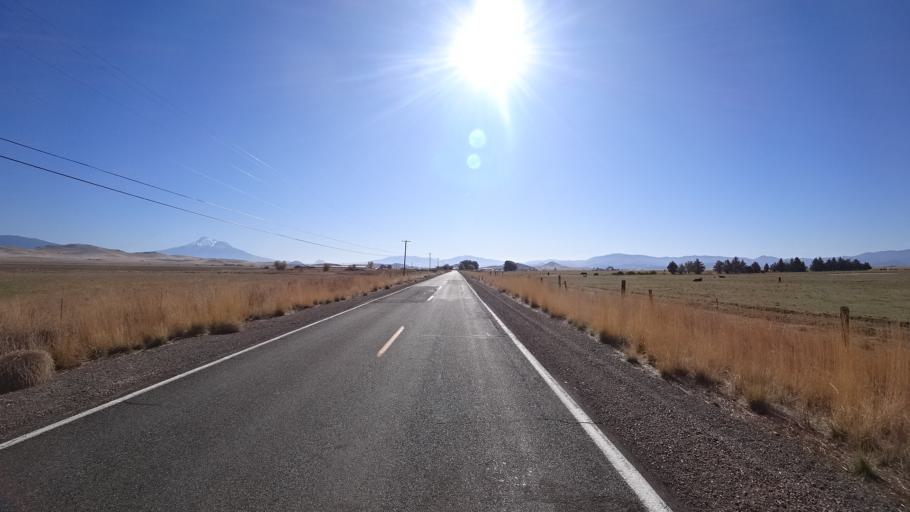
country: US
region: California
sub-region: Siskiyou County
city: Montague
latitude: 41.7879
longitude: -122.4723
